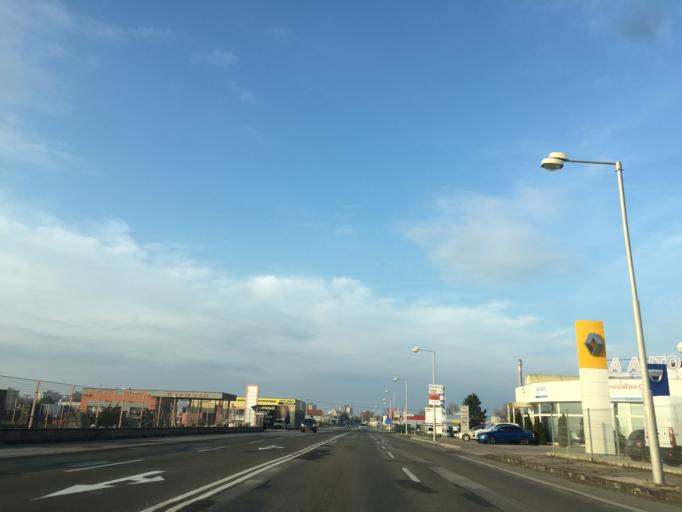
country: SK
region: Nitriansky
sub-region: Okres Nove Zamky
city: Nove Zamky
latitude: 47.9729
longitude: 18.1812
